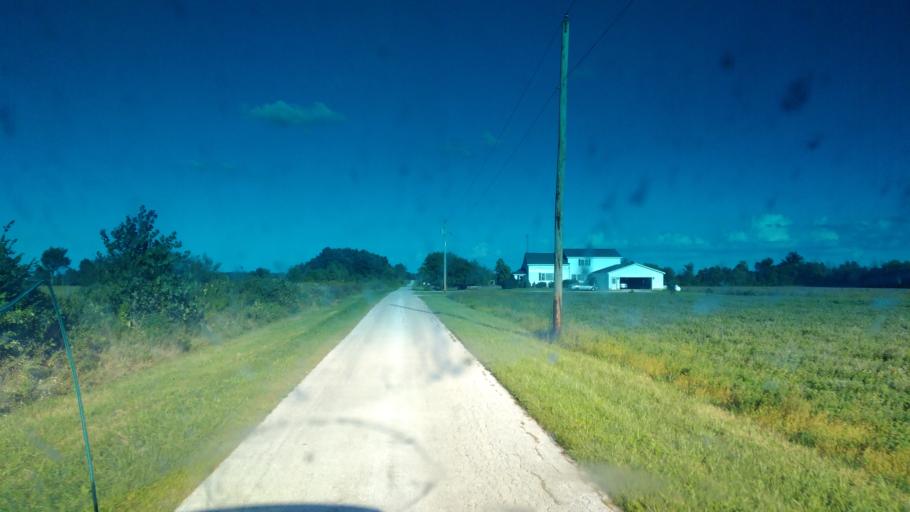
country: US
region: Ohio
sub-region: Wyandot County
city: Carey
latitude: 40.9413
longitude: -83.4431
